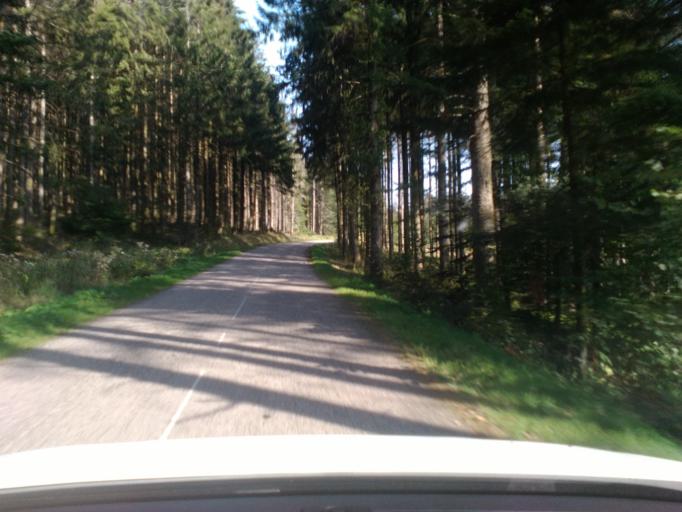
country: FR
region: Lorraine
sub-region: Departement des Vosges
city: Senones
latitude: 48.3387
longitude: 7.0479
